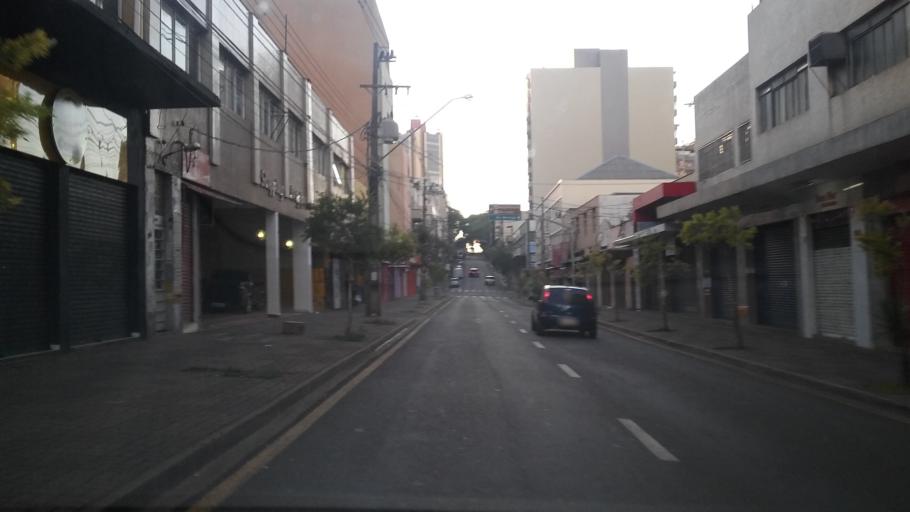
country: BR
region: Parana
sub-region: Londrina
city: Londrina
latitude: -23.3098
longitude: -51.1616
